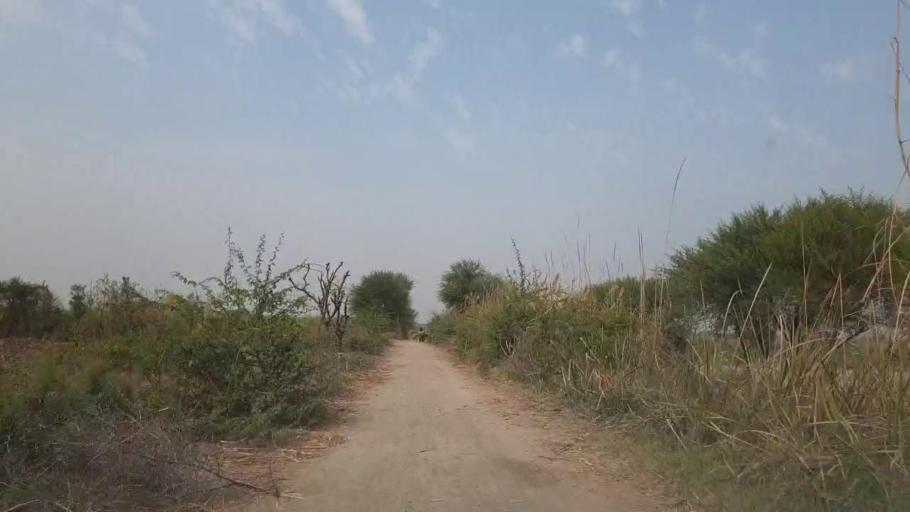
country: PK
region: Sindh
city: Mirpur Khas
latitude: 25.5645
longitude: 69.1052
